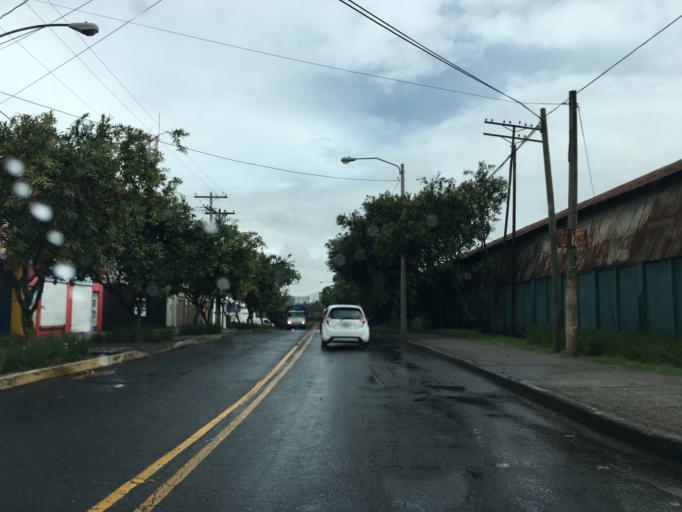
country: GT
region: Guatemala
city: Guatemala City
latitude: 14.6283
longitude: -90.5112
